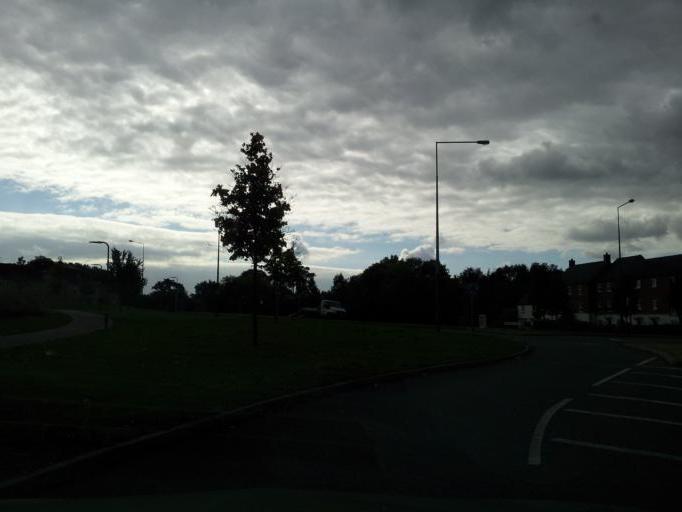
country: GB
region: England
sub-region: Milton Keynes
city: Shenley Church End
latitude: 52.0022
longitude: -0.8070
